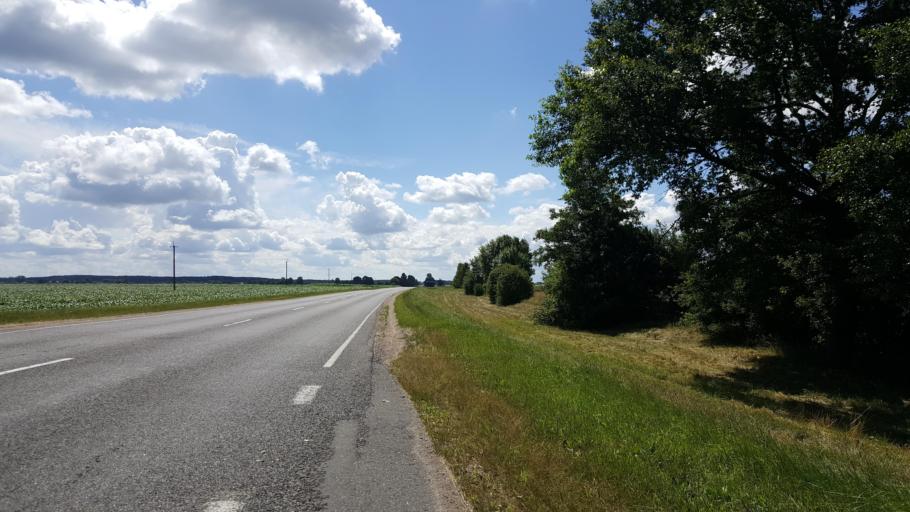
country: BY
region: Brest
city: Kamyanyets
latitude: 52.3706
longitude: 23.8837
